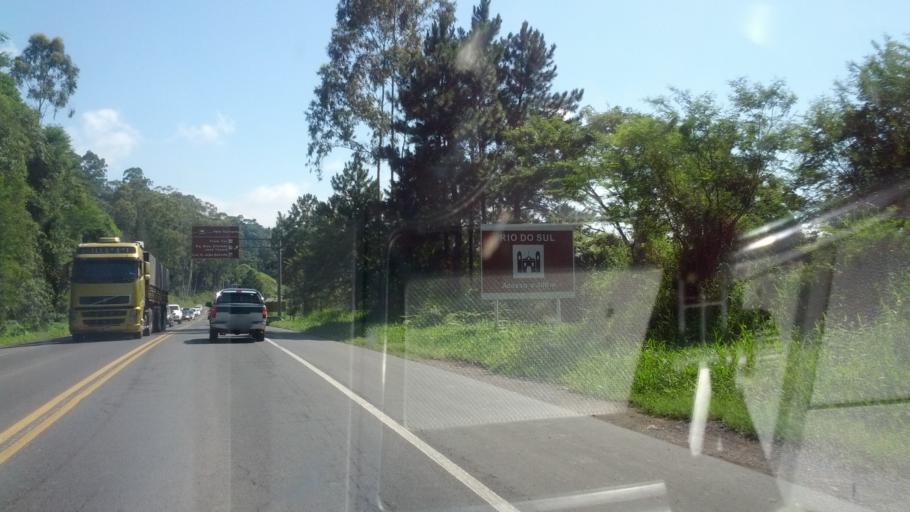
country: BR
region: Santa Catarina
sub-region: Rio Do Sul
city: Rio do Sul
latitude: -27.2256
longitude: -49.6657
